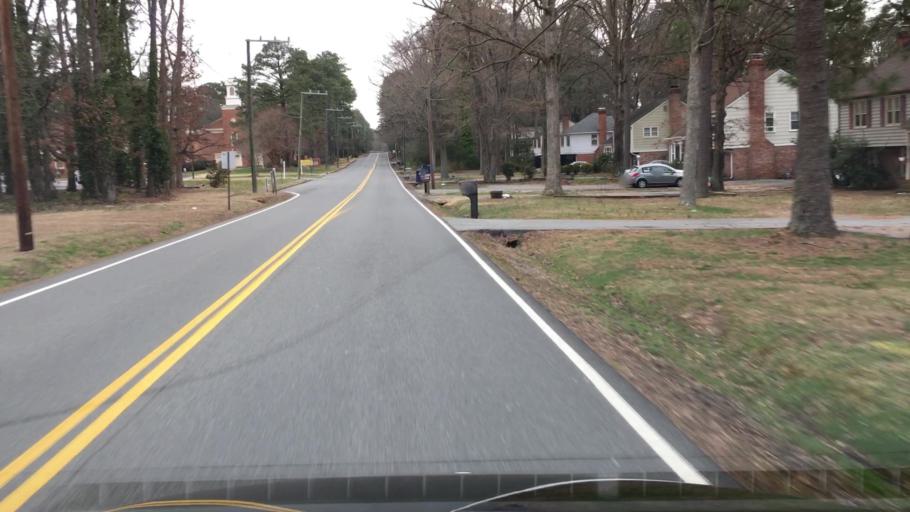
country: US
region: Virginia
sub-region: Henrico County
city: Tuckahoe
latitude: 37.5883
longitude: -77.5792
